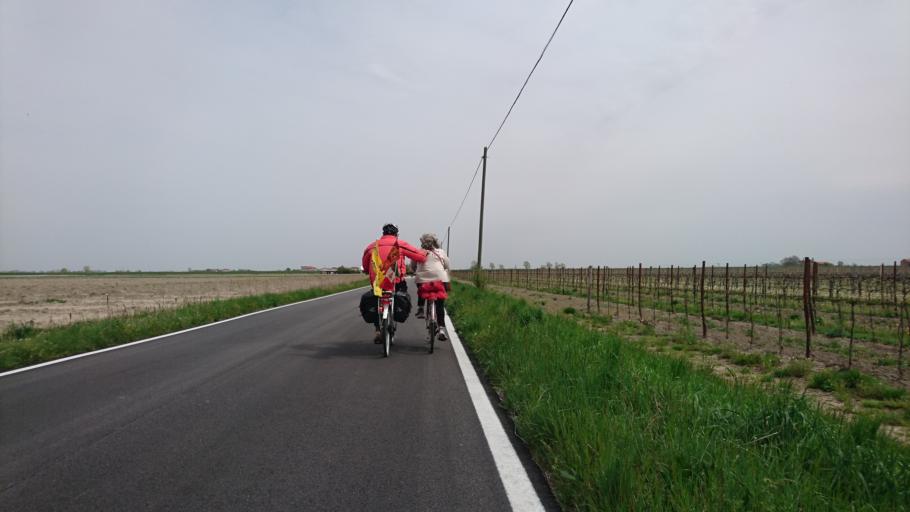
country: IT
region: Veneto
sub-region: Provincia di Venezia
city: La Salute di Livenza
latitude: 45.6662
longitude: 12.8445
